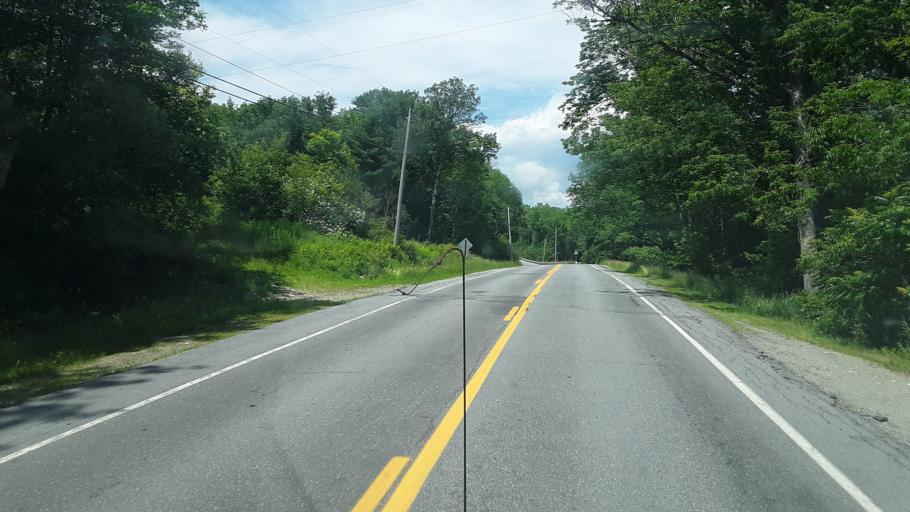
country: US
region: Maine
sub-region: Hancock County
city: Bucksport
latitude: 44.5687
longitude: -68.8091
